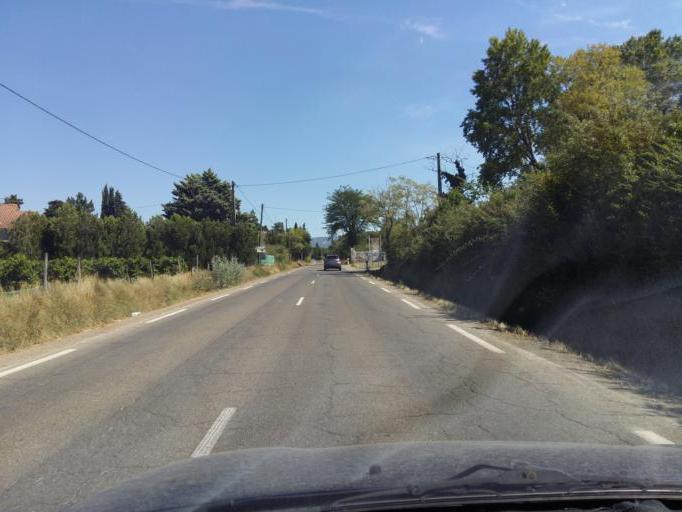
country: FR
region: Provence-Alpes-Cote d'Azur
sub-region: Departement du Vaucluse
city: Carpentras
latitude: 44.0403
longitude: 5.0650
